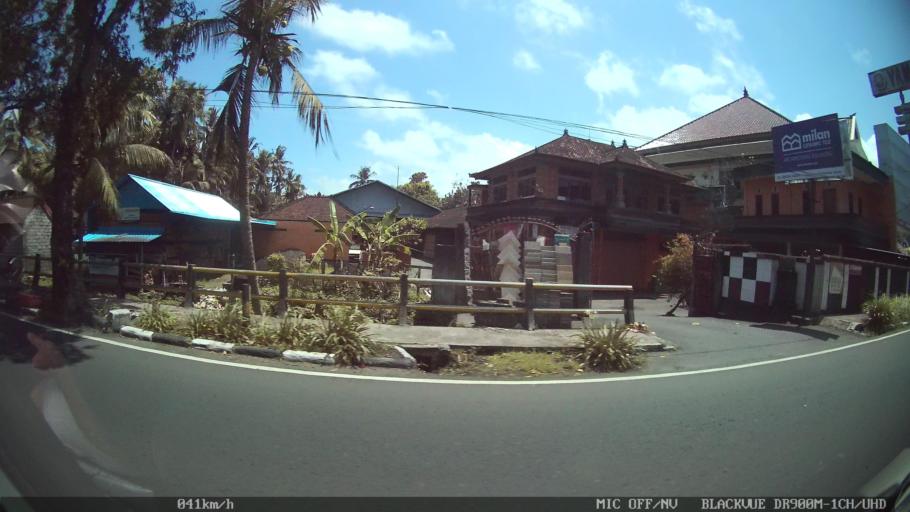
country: ID
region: Bali
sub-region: Kabupaten Gianyar
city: Ubud
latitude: -8.5551
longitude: 115.3026
